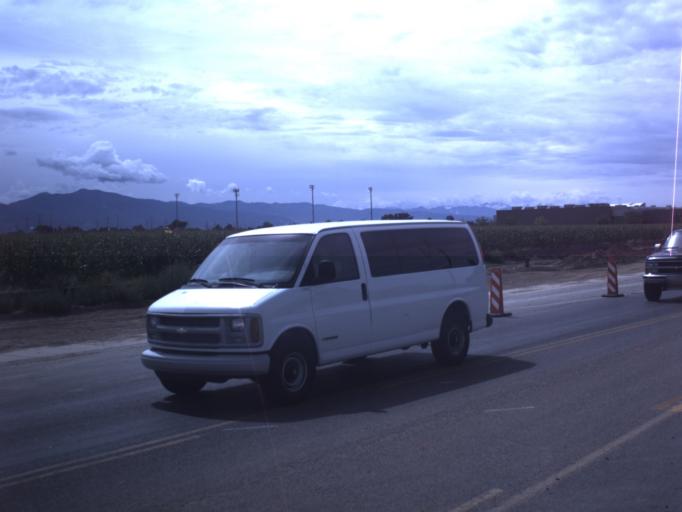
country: US
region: Utah
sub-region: Davis County
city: Syracuse
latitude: 41.1098
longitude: -112.0646
